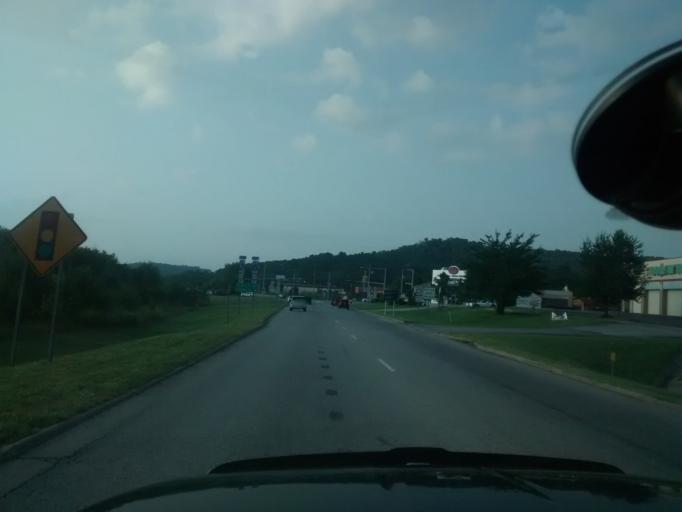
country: US
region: Arkansas
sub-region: Washington County
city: Fayetteville
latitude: 36.0556
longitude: -94.1964
